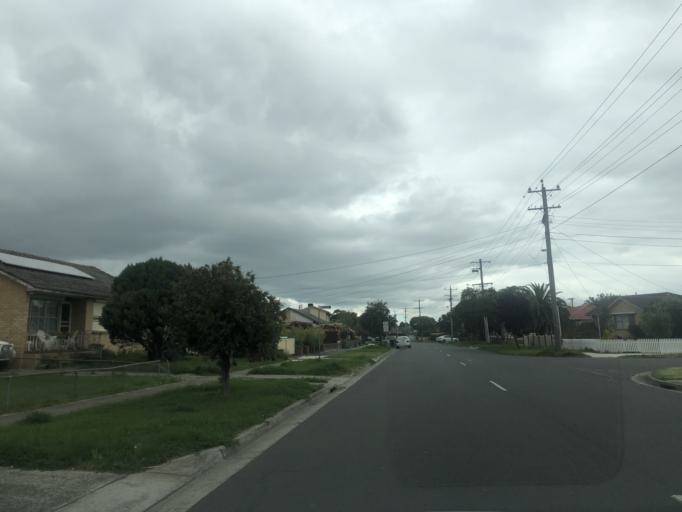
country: AU
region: Victoria
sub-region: Casey
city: Doveton
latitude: -37.9802
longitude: 145.2366
